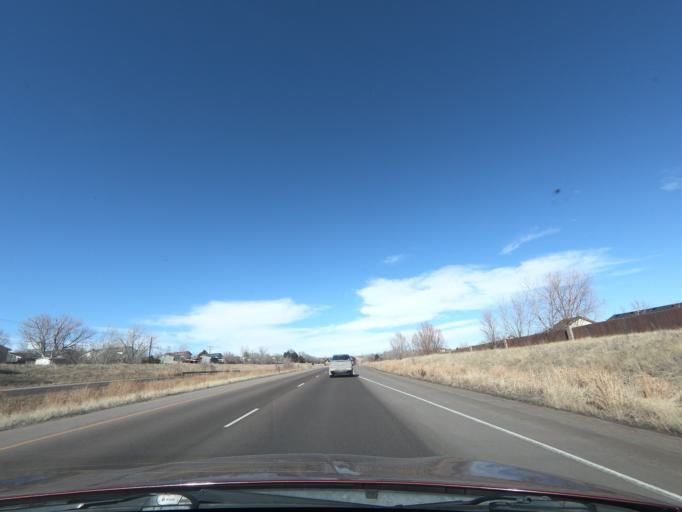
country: US
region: Colorado
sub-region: El Paso County
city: Security-Widefield
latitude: 38.7260
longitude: -104.6825
